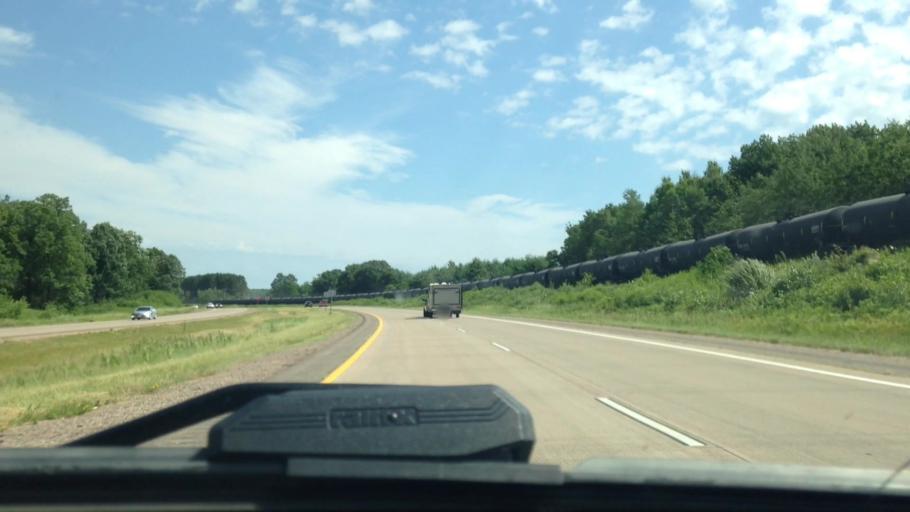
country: US
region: Wisconsin
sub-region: Washburn County
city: Spooner
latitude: 45.8664
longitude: -91.8326
